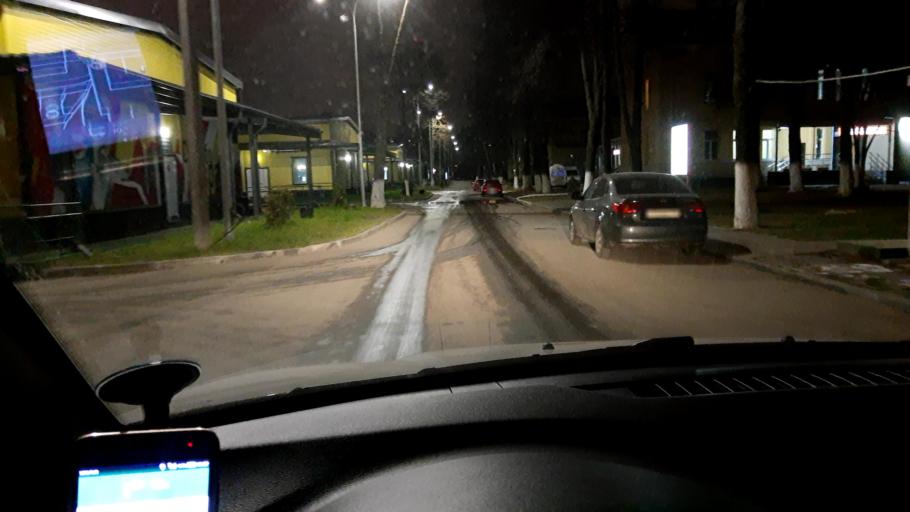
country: RU
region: Nizjnij Novgorod
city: Gorbatovka
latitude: 56.2497
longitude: 43.8325
